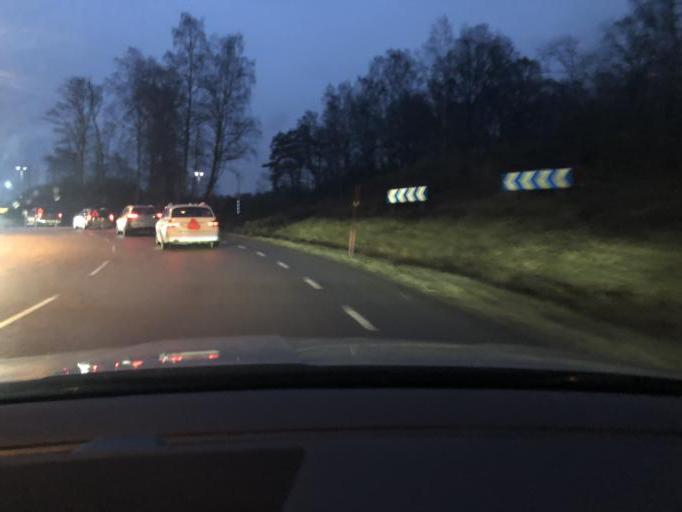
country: SE
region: Joenkoeping
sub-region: Jonkopings Kommun
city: Jonkoping
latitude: 57.7633
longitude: 14.1997
